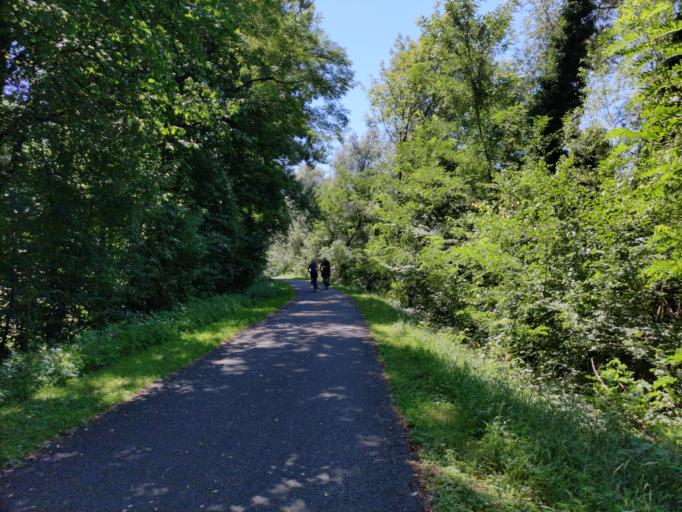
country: AT
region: Styria
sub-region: Politischer Bezirk Leibnitz
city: Retznei
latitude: 46.7320
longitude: 15.5781
